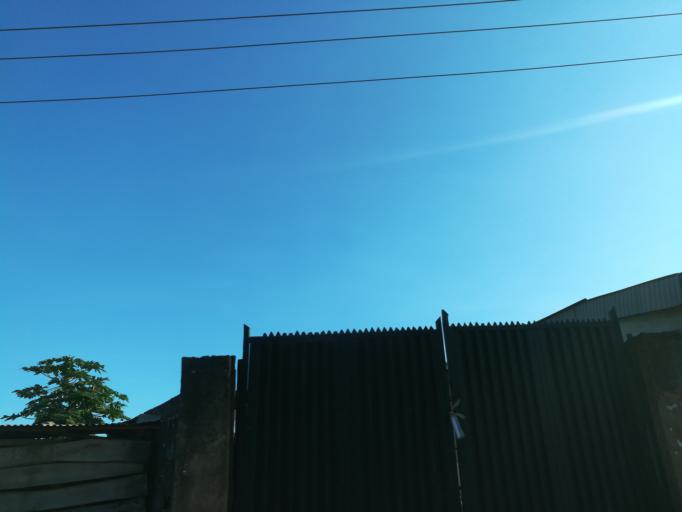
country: NG
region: Lagos
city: Ikorodu
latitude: 6.5822
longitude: 3.5260
